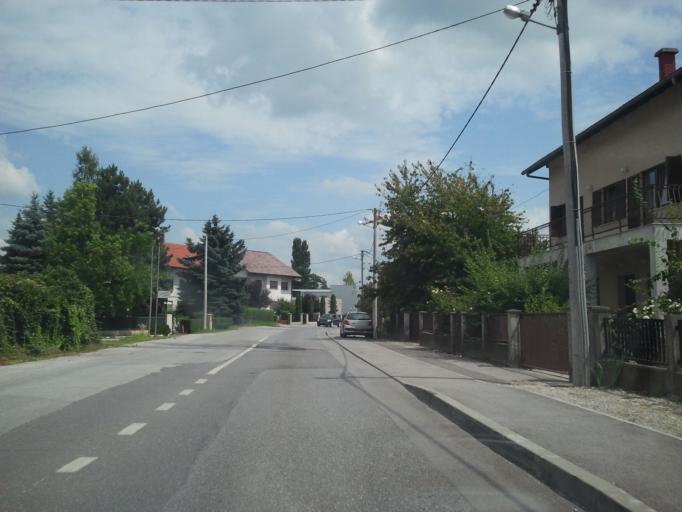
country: HR
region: Grad Zagreb
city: Zadvorsko
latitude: 45.7654
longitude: 15.9205
